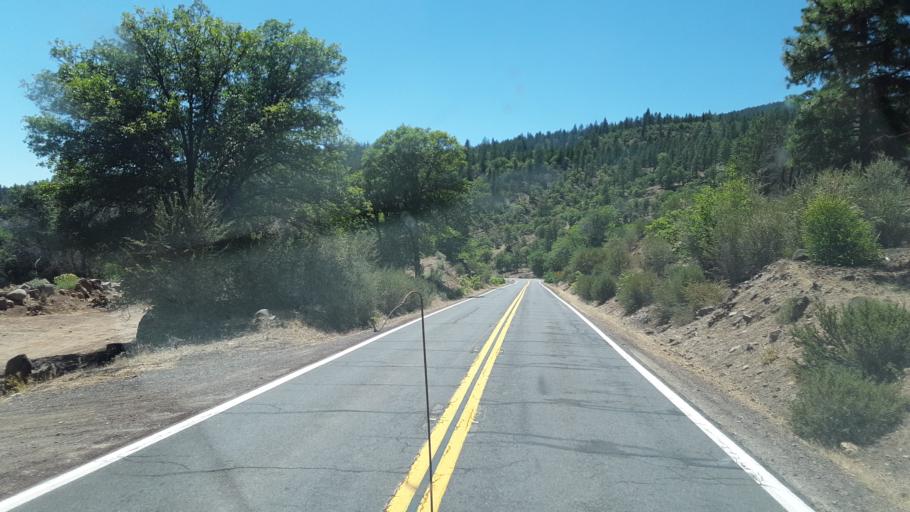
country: US
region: California
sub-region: Lassen County
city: Susanville
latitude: 40.4679
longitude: -120.6125
